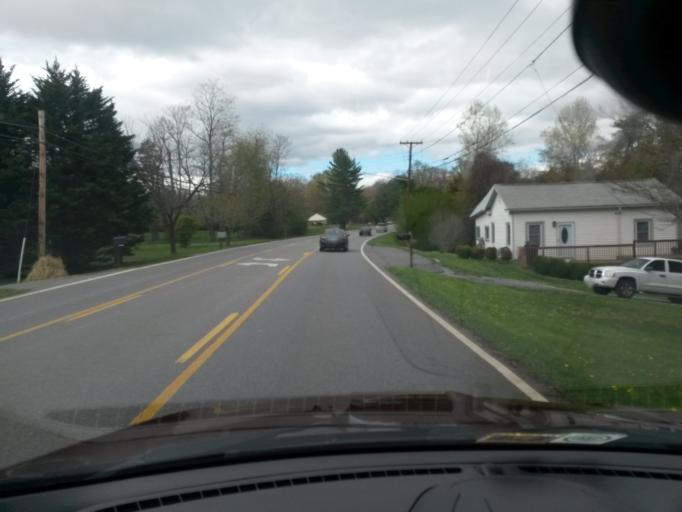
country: US
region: Virginia
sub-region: City of Lynchburg
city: West Lynchburg
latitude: 37.4429
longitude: -79.2411
